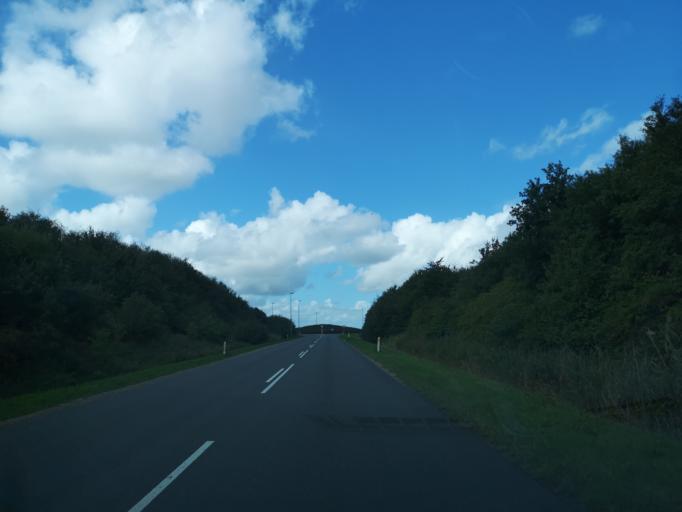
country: DK
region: Central Jutland
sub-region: Holstebro Kommune
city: Holstebro
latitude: 56.3891
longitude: 8.6006
